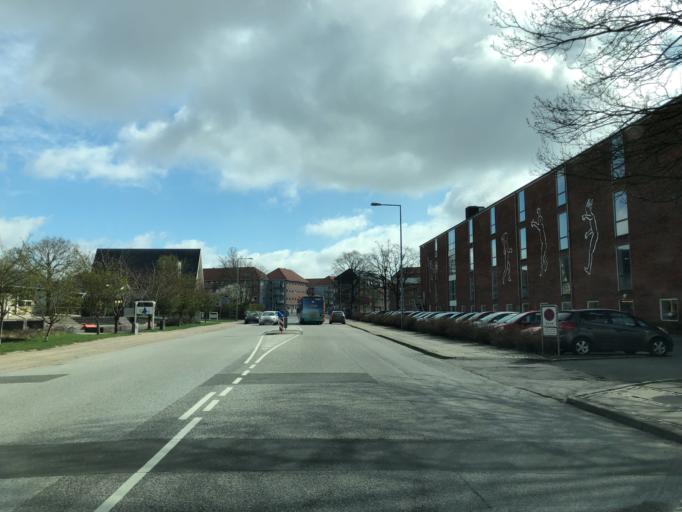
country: DK
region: North Denmark
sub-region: Alborg Kommune
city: Aalborg
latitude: 57.0554
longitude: 9.8895
